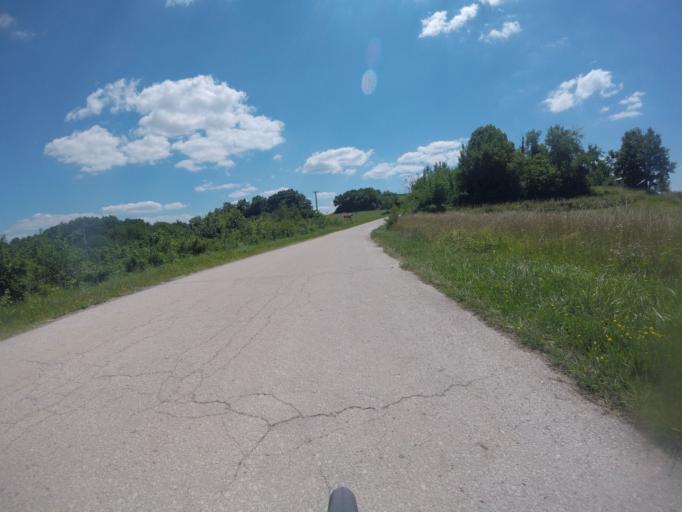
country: HR
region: Karlovacka
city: Ozalj
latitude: 45.6716
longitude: 15.4077
